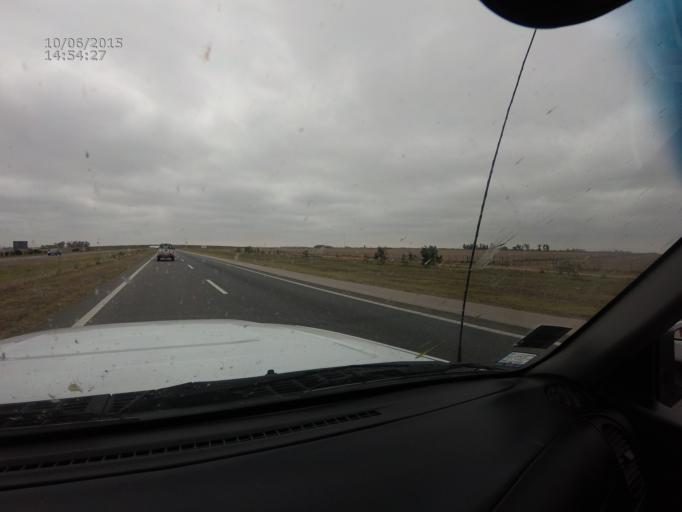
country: AR
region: Cordoba
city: Oncativo
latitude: -31.8542
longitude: -63.6845
